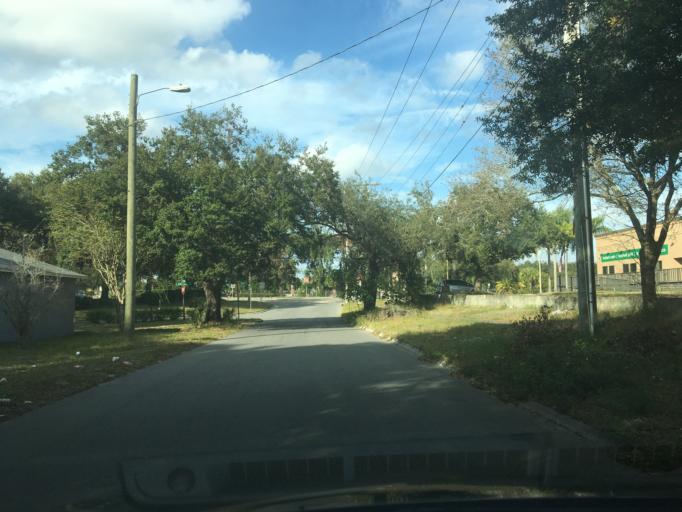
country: US
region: Florida
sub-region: Hillsborough County
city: Temple Terrace
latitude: 28.0316
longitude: -82.4144
